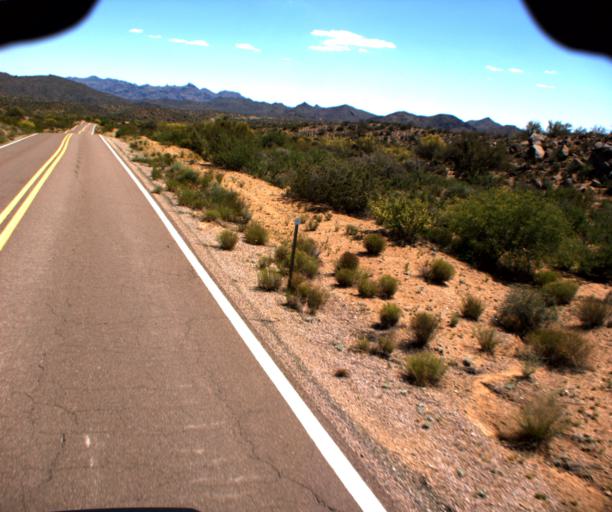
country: US
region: Arizona
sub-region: Yavapai County
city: Bagdad
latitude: 34.4580
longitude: -113.2434
